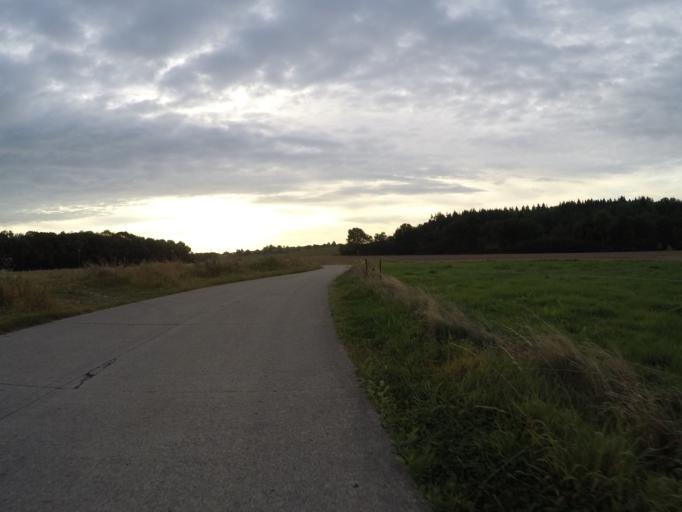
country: BE
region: Wallonia
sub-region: Province de Namur
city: Assesse
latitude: 50.3427
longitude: 5.0369
